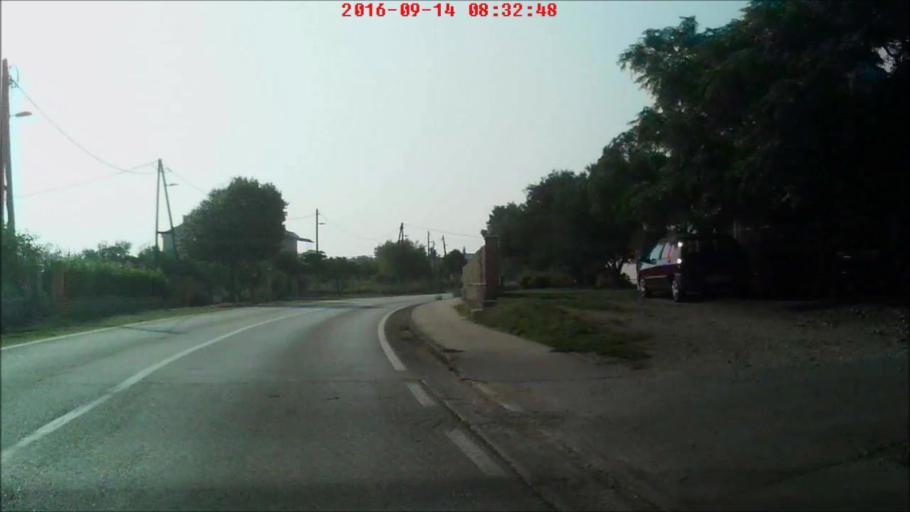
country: HR
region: Zadarska
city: Policnik
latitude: 44.1608
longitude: 15.3084
